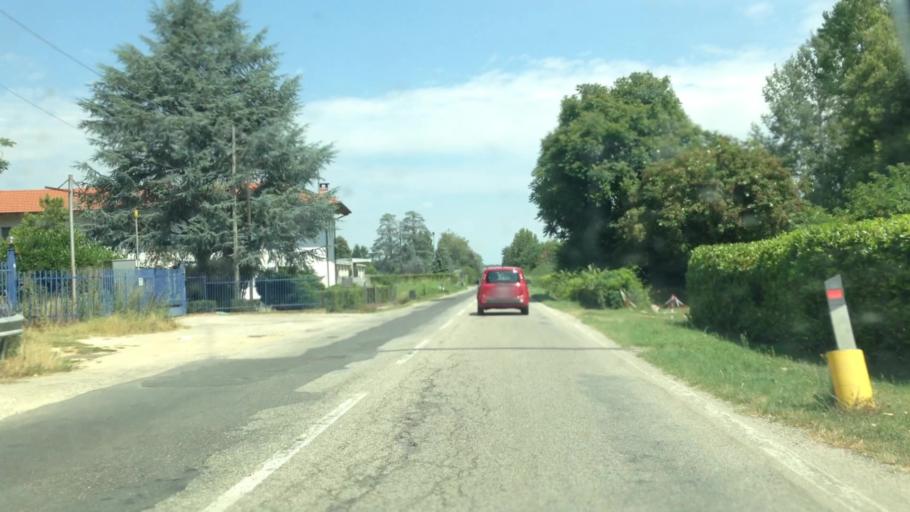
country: IT
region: Piedmont
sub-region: Provincia di Asti
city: Asti
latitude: 44.9288
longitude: 8.2256
